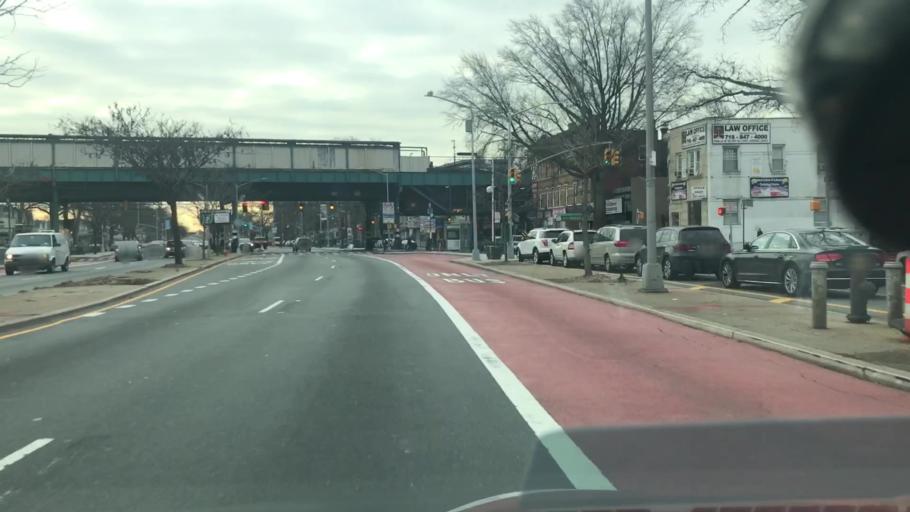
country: US
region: New York
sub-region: Queens County
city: Borough of Queens
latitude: 40.6945
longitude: -73.8526
